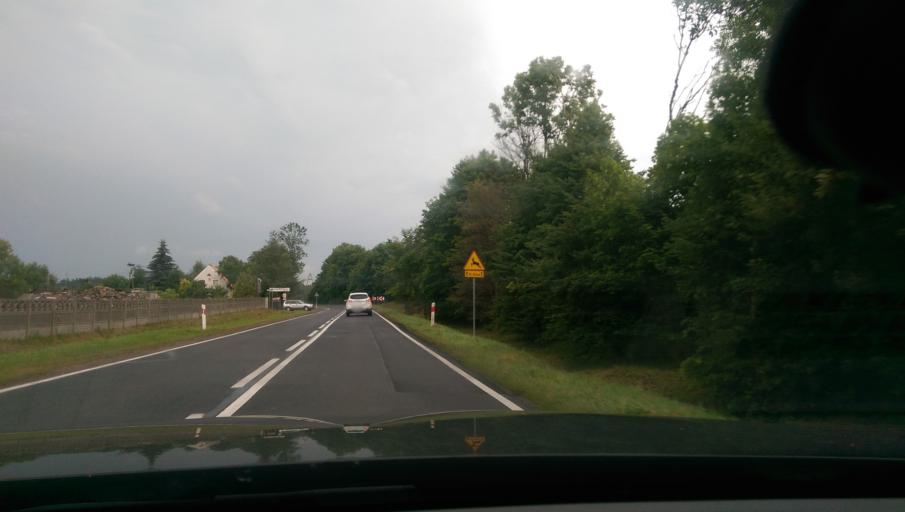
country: PL
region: Warmian-Masurian Voivodeship
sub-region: Powiat szczycienski
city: Szczytno
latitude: 53.5471
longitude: 20.9887
